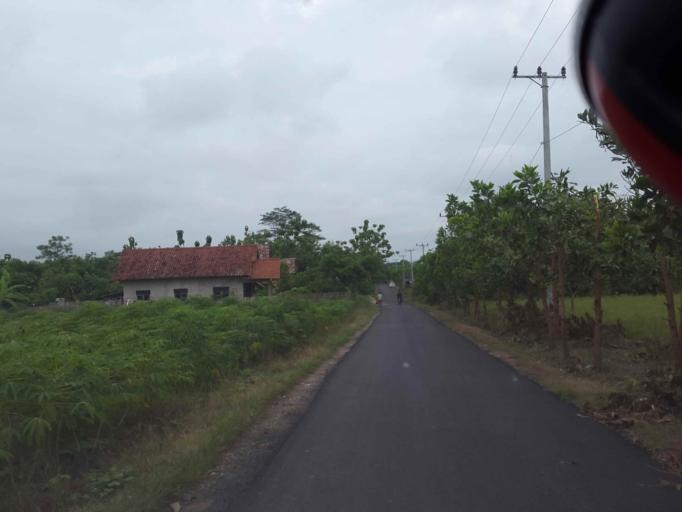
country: ID
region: Lampung
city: Natar
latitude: -5.2648
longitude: 105.2057
